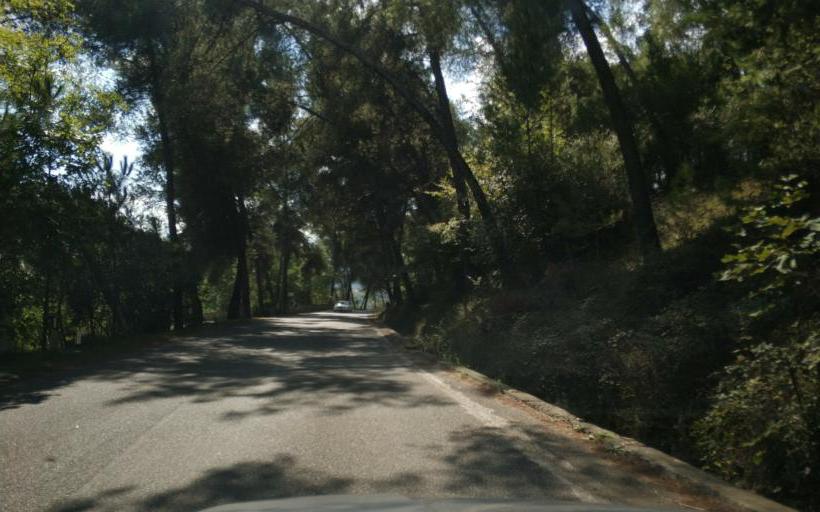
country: AL
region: Durres
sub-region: Rrethi i Krujes
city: Kruje
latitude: 41.4895
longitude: 19.7677
